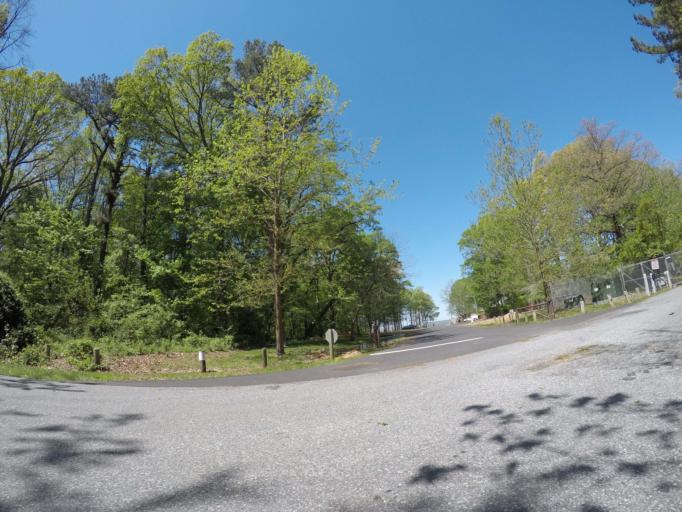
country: US
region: Maryland
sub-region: Queen Anne's County
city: Stevensville
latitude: 38.9535
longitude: -76.3534
